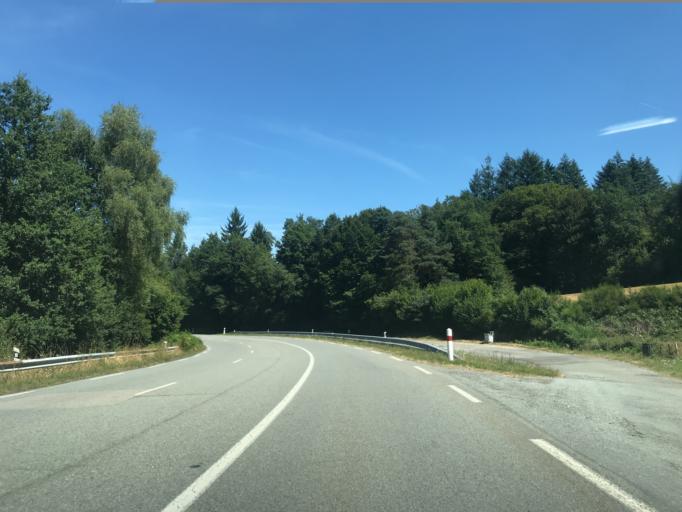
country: FR
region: Limousin
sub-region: Departement de la Correze
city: Egletons
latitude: 45.4113
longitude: 2.0539
